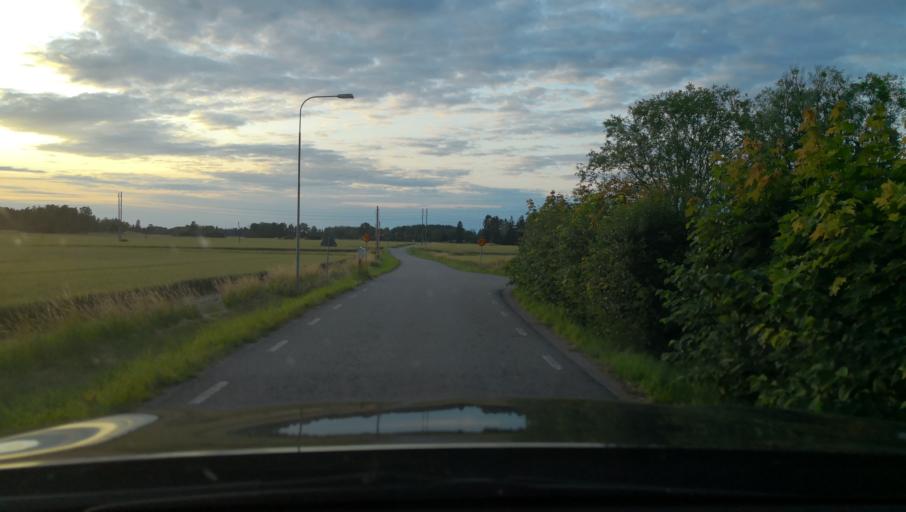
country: SE
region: Uppsala
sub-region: Uppsala Kommun
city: Vattholma
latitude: 60.0396
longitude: 17.6644
